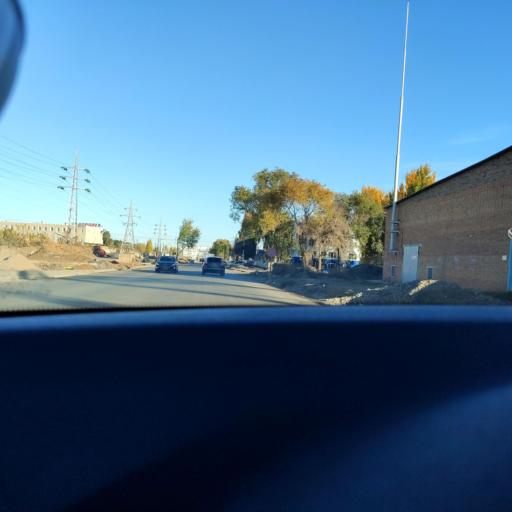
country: RU
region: Samara
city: Samara
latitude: 53.1949
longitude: 50.2351
